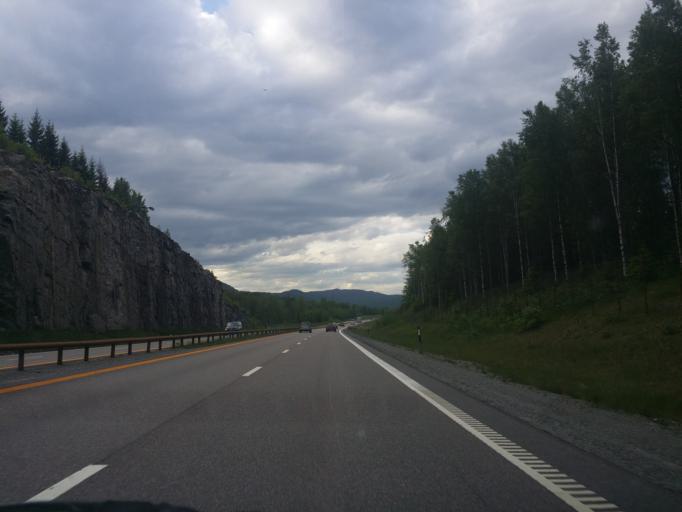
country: NO
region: Akershus
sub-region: Eidsvoll
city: Eidsvoll
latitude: 60.3557
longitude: 11.2068
